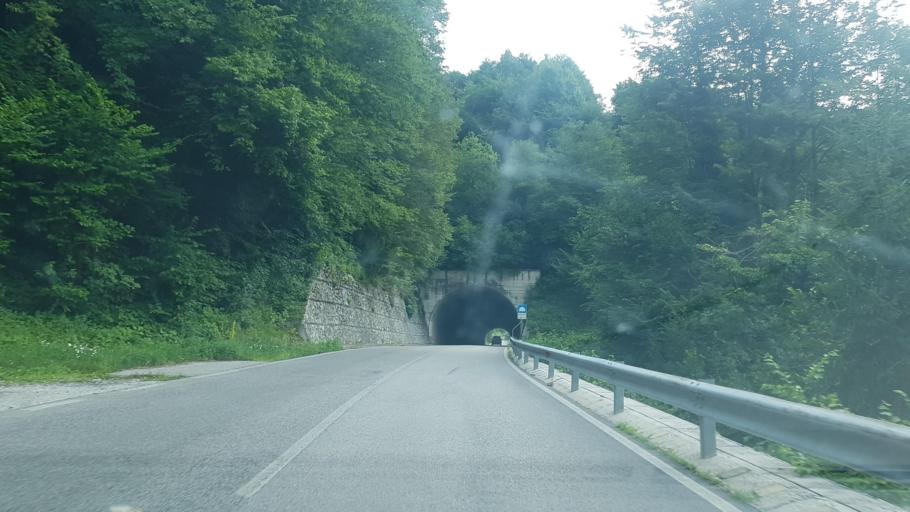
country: IT
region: Friuli Venezia Giulia
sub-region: Provincia di Udine
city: Paularo
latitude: 46.4998
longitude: 13.1097
